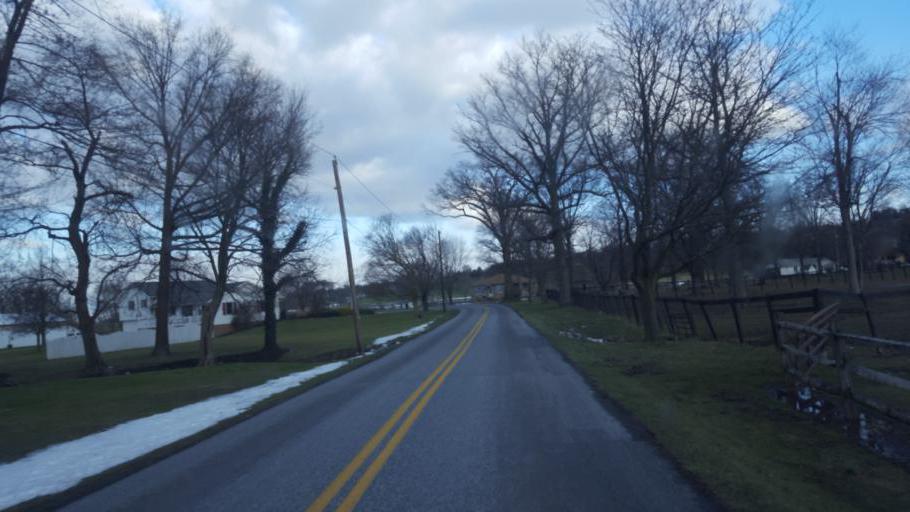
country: US
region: Pennsylvania
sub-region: Lancaster County
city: New Holland
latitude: 40.0692
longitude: -76.0603
